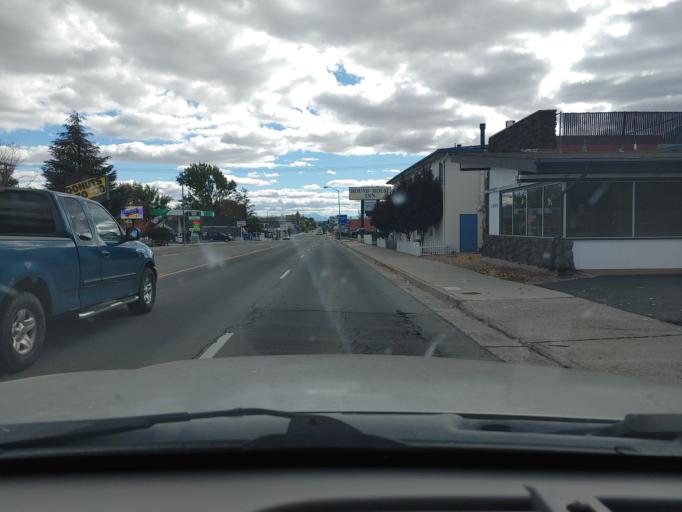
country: US
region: Nevada
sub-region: Carson City
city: Carson City
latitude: 39.1734
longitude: -119.7671
